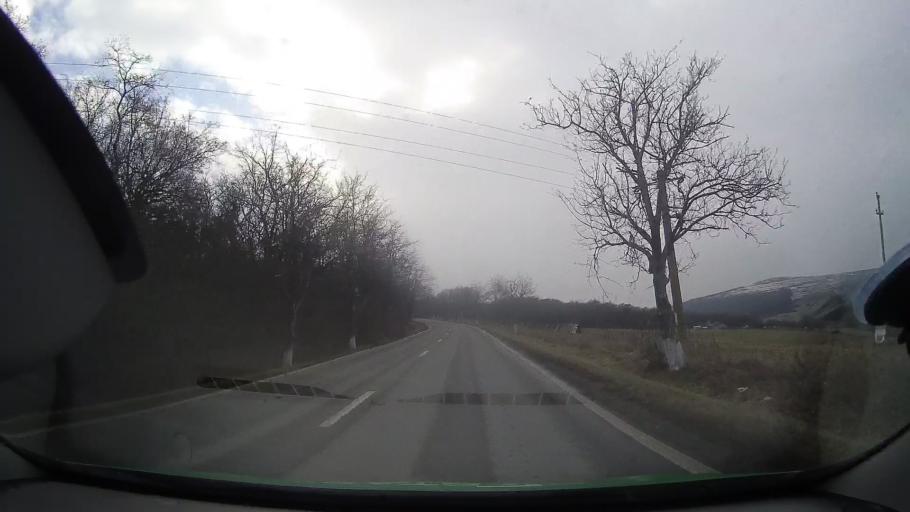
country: RO
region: Mures
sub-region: Municipiul Tarnaveni
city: Bobohalma
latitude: 46.3526
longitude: 24.2664
